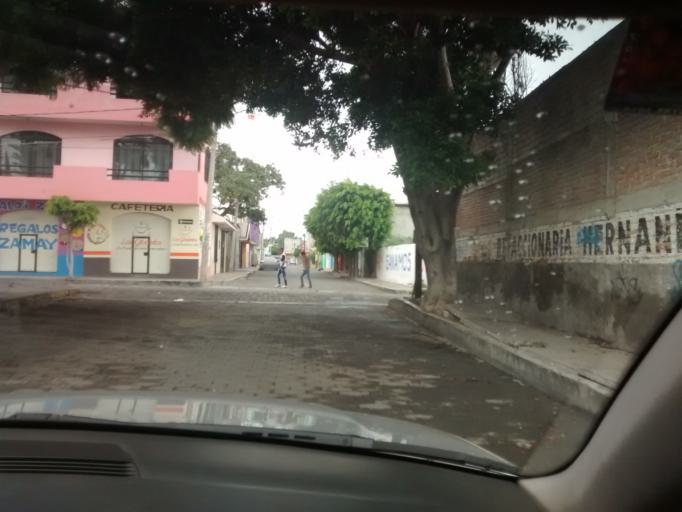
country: MX
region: Puebla
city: Tehuacan
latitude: 18.4544
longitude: -97.3952
